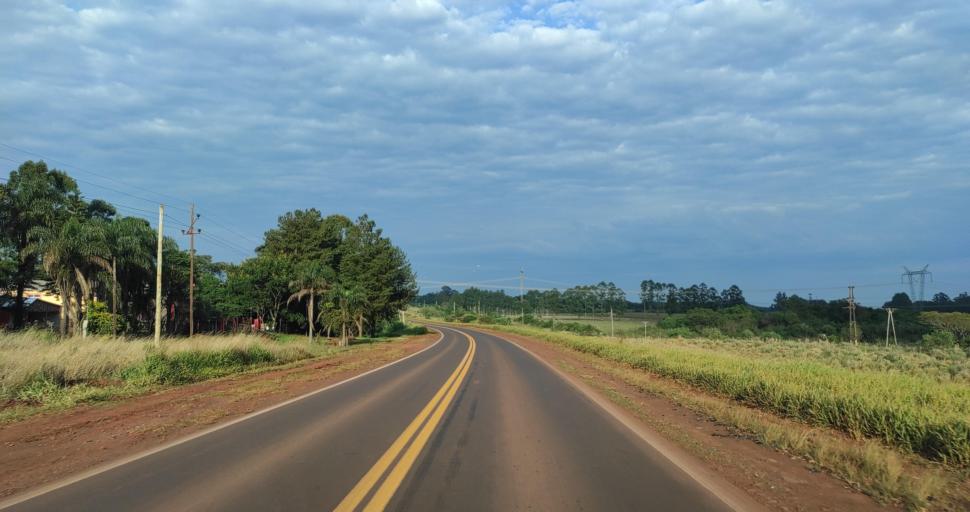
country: AR
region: Corrientes
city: Gobernador Ingeniero Valentin Virasoro
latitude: -27.9555
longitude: -55.9986
